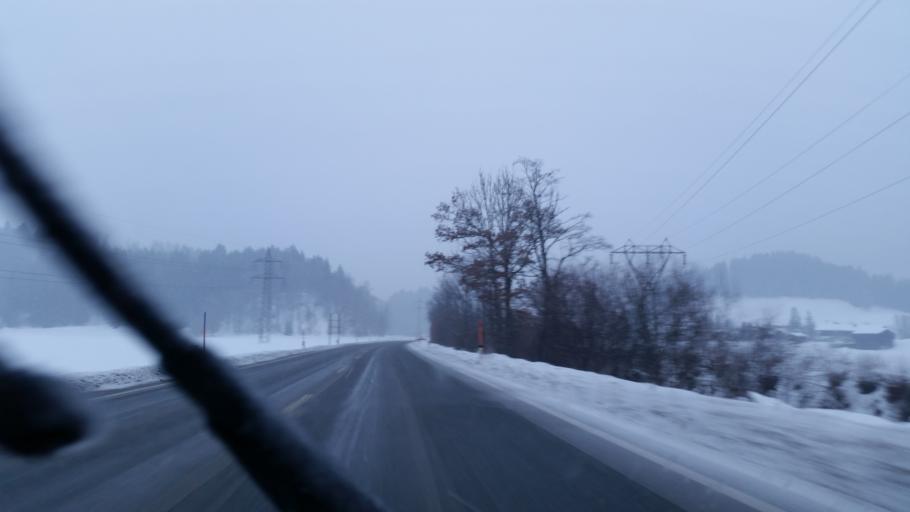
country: AT
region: Tyrol
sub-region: Politischer Bezirk Kitzbuhel
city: Sankt Johann in Tirol
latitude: 47.5195
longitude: 12.4011
